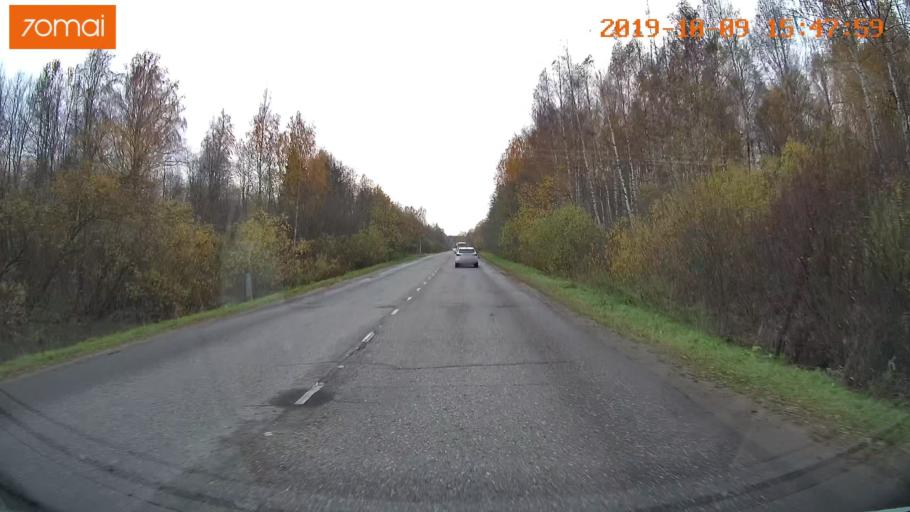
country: RU
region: Kostroma
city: Oktyabr'skiy
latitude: 57.8142
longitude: 41.0215
